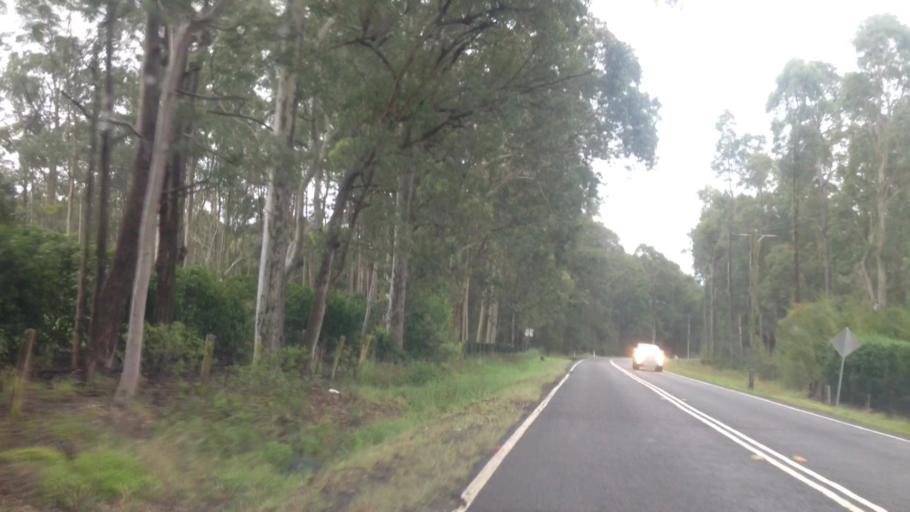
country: AU
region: New South Wales
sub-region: Wyong Shire
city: Little Jilliby
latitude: -33.2544
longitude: 151.3972
